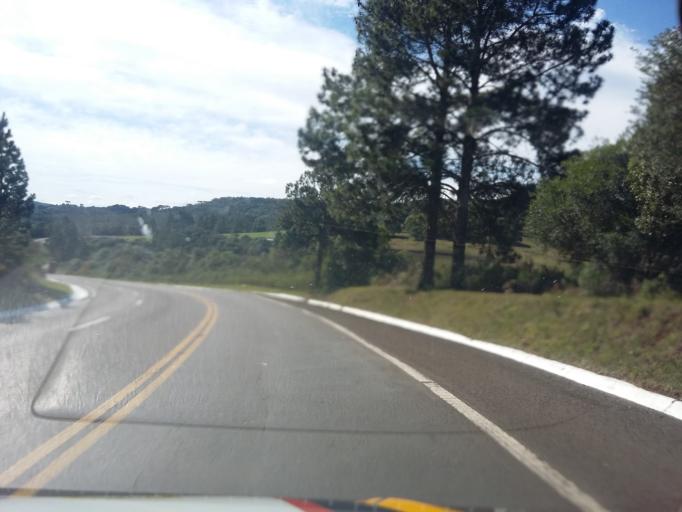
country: BR
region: Rio Grande do Sul
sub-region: Vacaria
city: Vacaria
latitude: -28.5759
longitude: -51.0140
